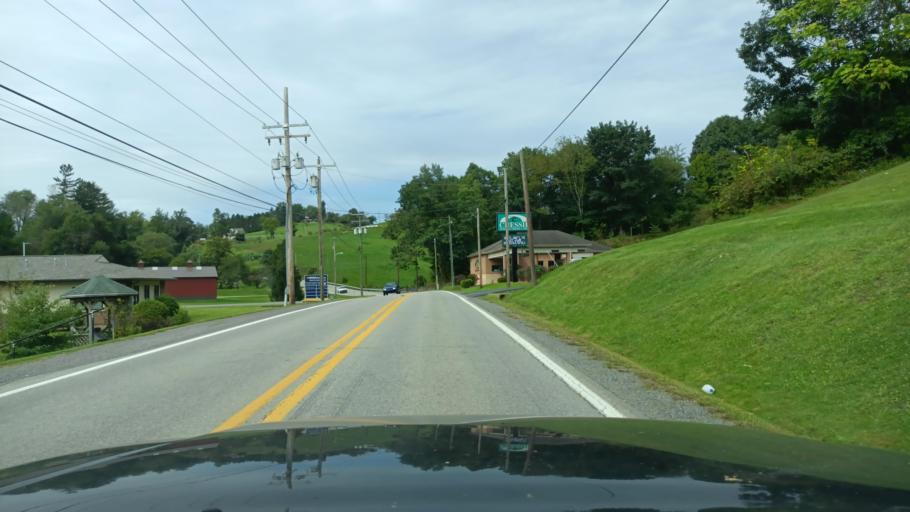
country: US
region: West Virginia
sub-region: Taylor County
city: Grafton
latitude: 39.3483
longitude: -80.0080
